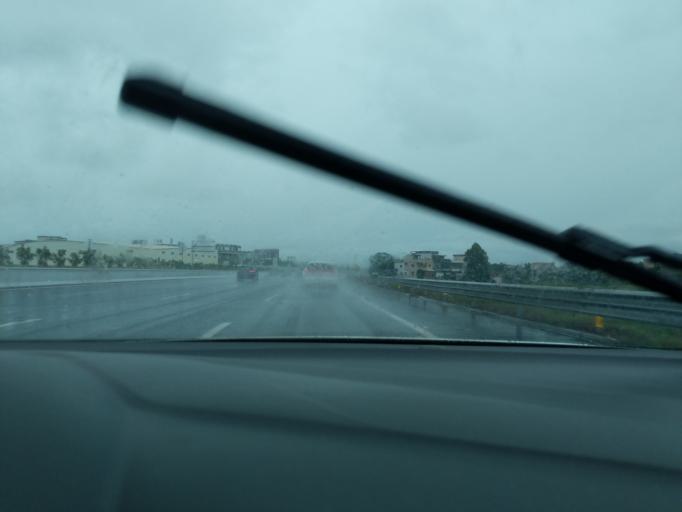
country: CN
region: Guangdong
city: Shuikou
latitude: 22.4808
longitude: 112.7732
